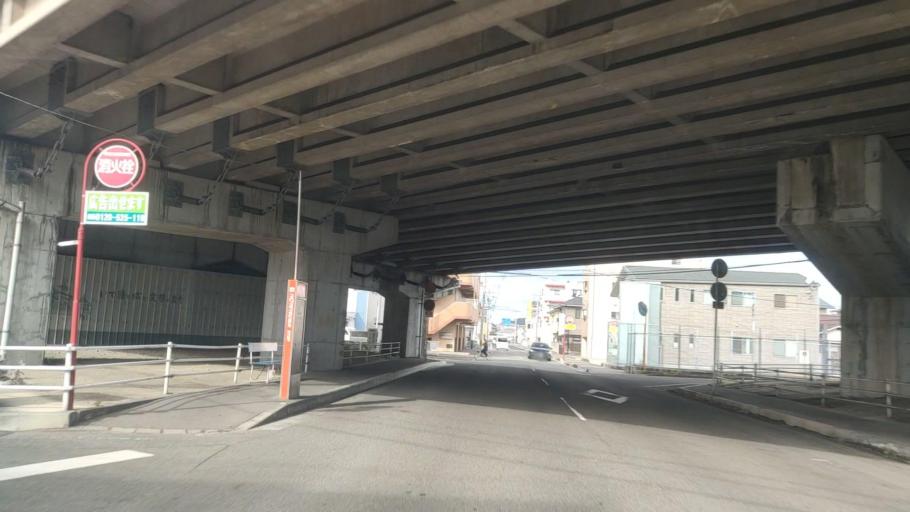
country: JP
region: Ehime
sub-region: Shikoku-chuo Shi
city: Matsuyama
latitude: 33.8216
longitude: 132.7589
